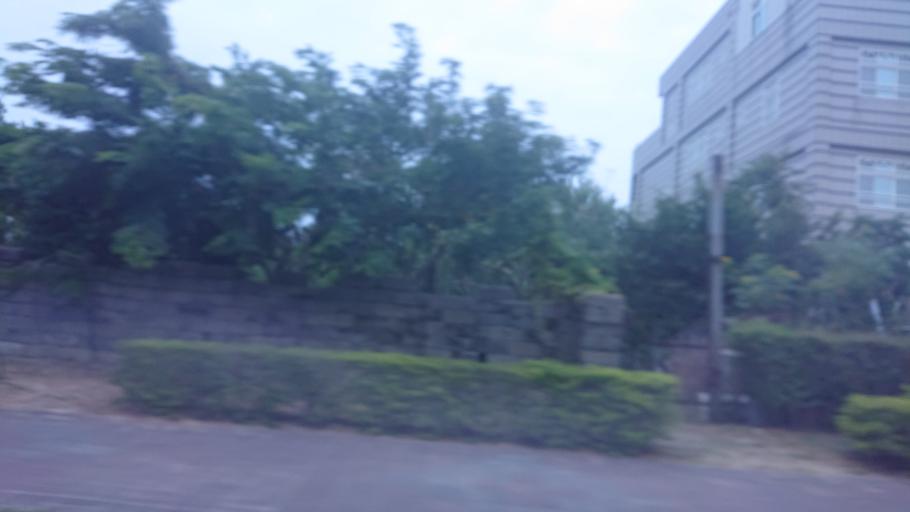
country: TW
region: Fukien
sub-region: Kinmen
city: Jincheng
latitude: 24.4380
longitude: 118.3119
